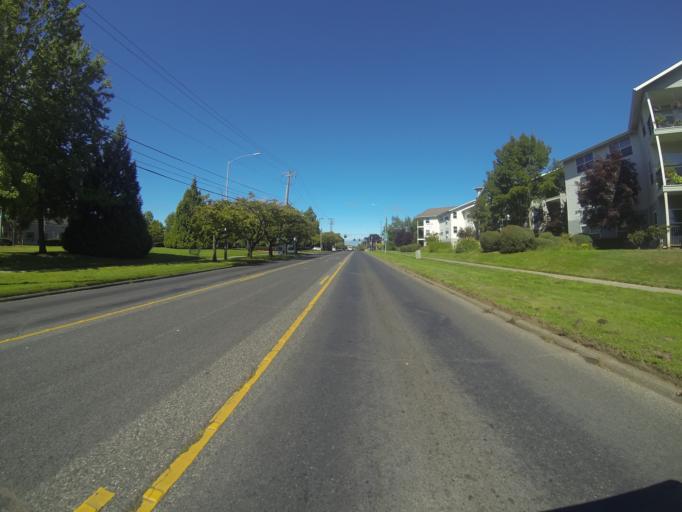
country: US
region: Washington
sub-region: Cowlitz County
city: Longview
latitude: 46.1352
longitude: -122.9251
